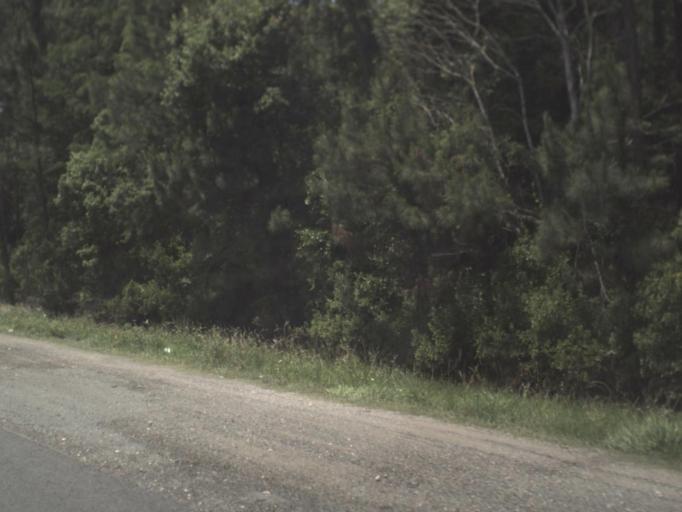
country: US
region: Florida
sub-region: Duval County
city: Baldwin
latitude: 30.2809
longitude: -81.9843
